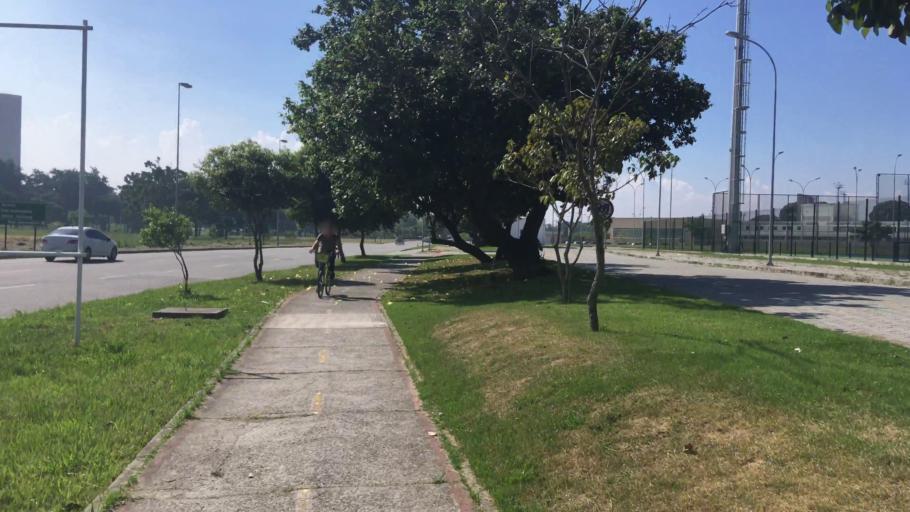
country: BR
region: Rio de Janeiro
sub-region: Rio De Janeiro
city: Rio de Janeiro
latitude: -22.8465
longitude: -43.2356
